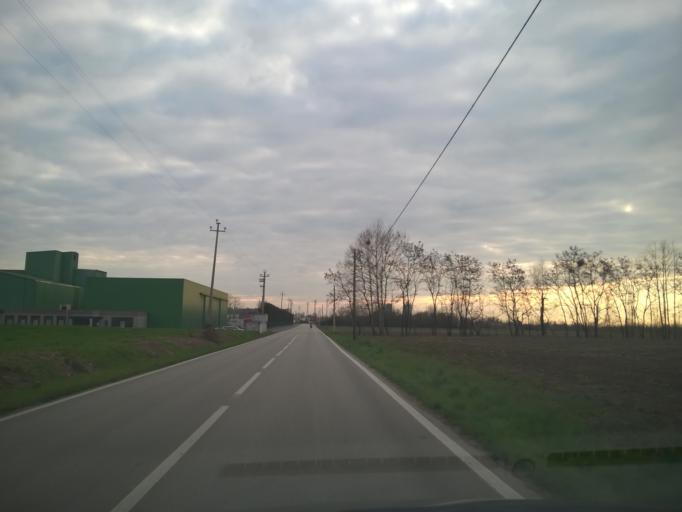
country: IT
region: Veneto
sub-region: Provincia di Vicenza
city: Novoledo
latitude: 45.6562
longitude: 11.5202
